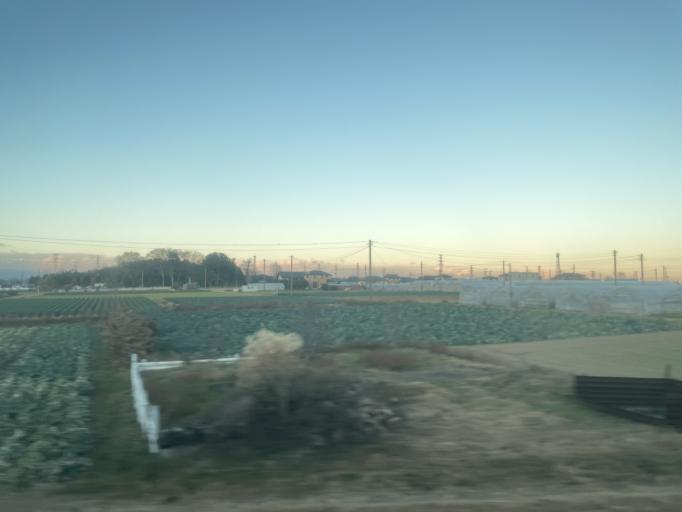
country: JP
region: Saitama
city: Honjo
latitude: 36.2133
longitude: 139.2243
